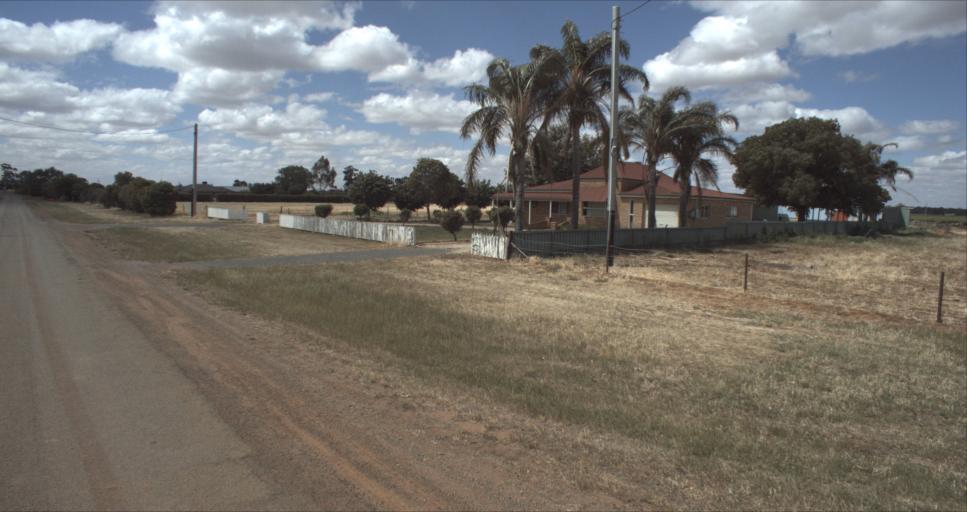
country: AU
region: New South Wales
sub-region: Leeton
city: Leeton
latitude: -34.5840
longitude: 146.3964
